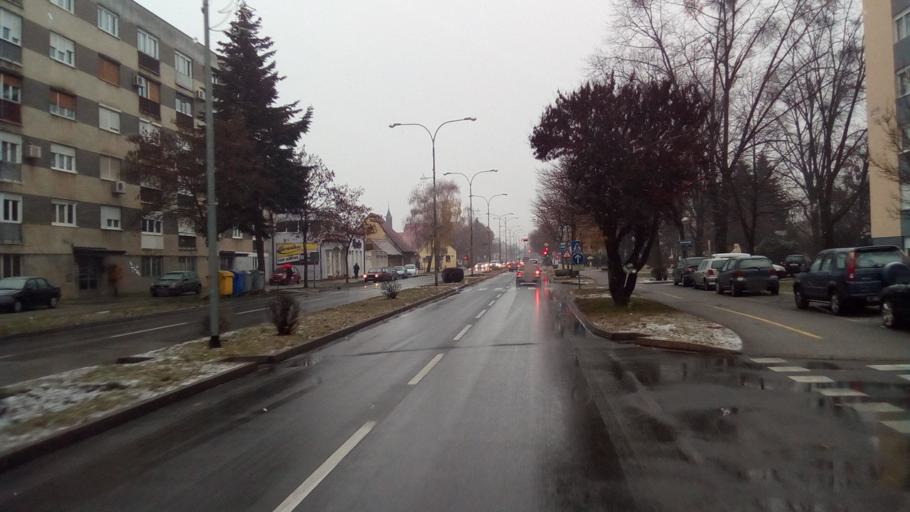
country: HR
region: Varazdinska
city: Varazdin
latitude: 46.3022
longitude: 16.3357
